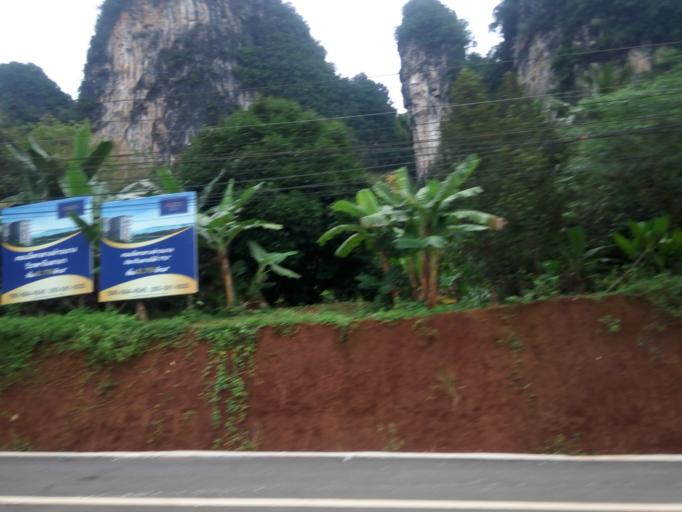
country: TH
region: Phangnga
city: Ban Ao Nang
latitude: 8.1757
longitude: 98.7907
